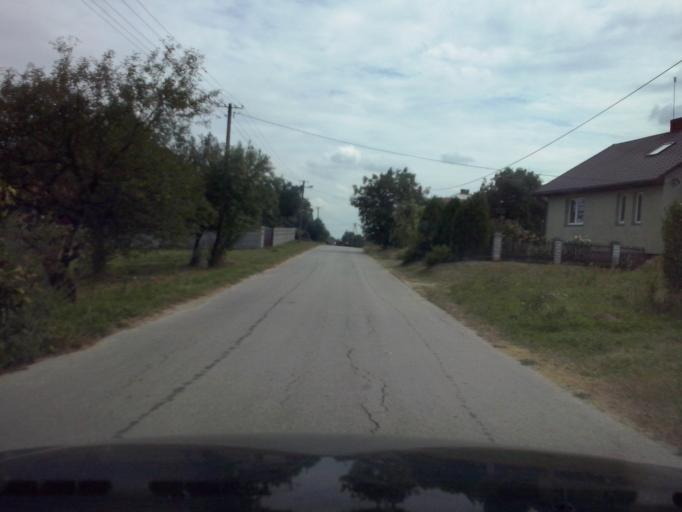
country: PL
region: Swietokrzyskie
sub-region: Powiat kielecki
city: Lagow
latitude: 50.7185
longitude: 21.1208
